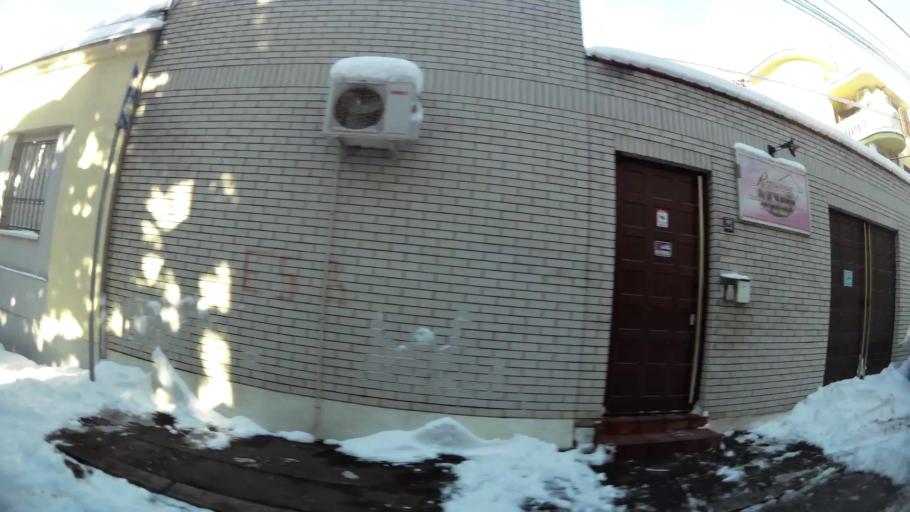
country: RS
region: Central Serbia
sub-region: Belgrade
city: Vracar
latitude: 44.7953
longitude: 20.4946
